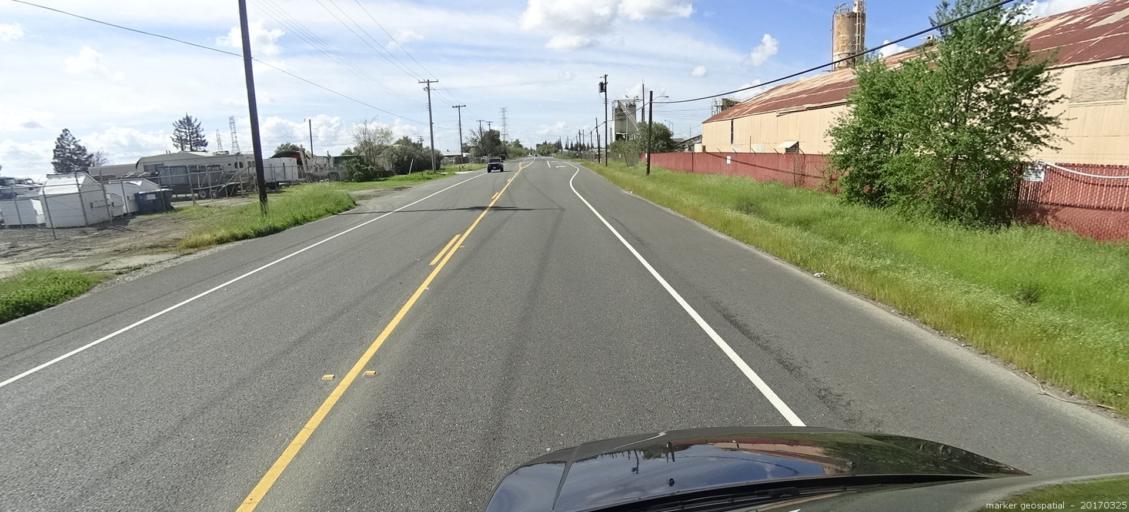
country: US
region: California
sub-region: Sacramento County
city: Rosemont
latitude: 38.5412
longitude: -121.3797
